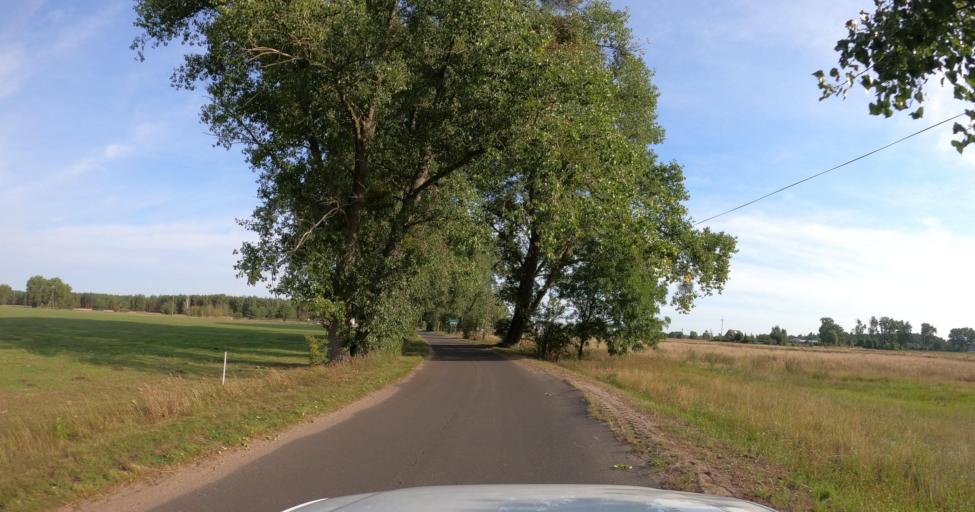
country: PL
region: West Pomeranian Voivodeship
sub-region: Powiat goleniowski
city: Goleniow
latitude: 53.5148
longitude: 14.7172
